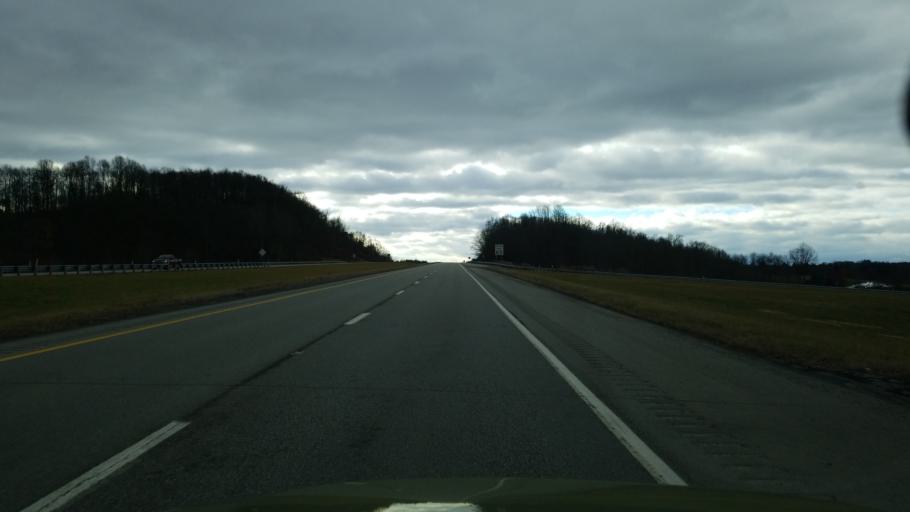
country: US
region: Pennsylvania
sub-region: Indiana County
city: Chevy Chase Heights
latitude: 40.6674
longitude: -79.1136
